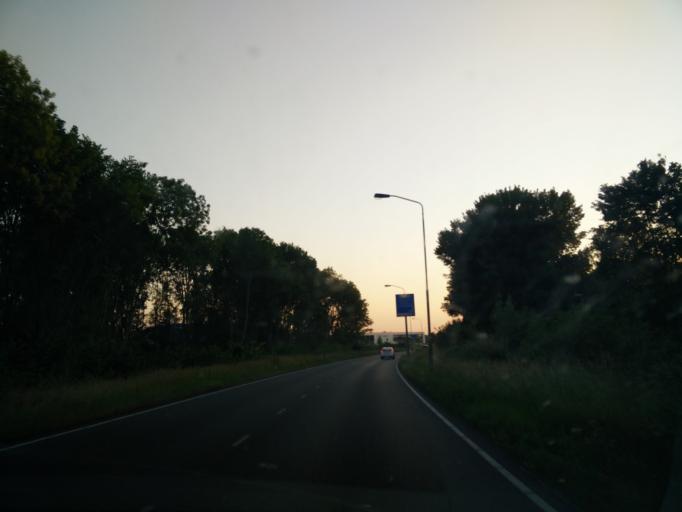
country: NL
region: North Brabant
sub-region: Gemeente Breda
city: Breda
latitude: 51.5999
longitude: 4.7466
